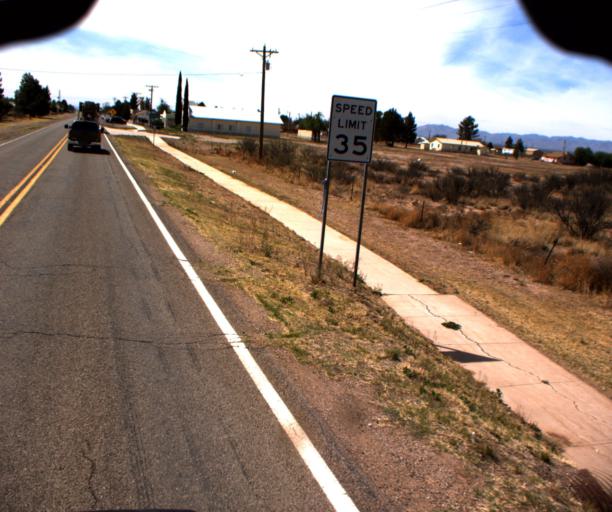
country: US
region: Arizona
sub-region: Cochise County
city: Bisbee
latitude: 31.6887
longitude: -109.6874
